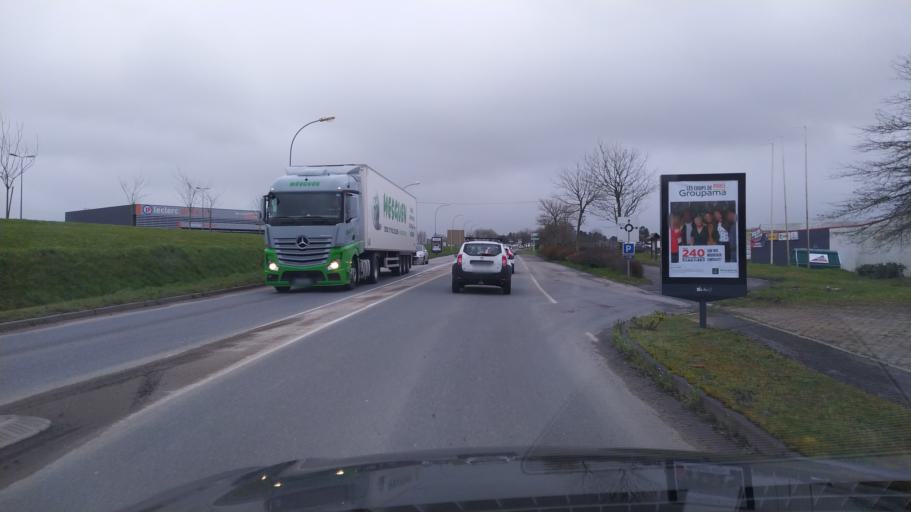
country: FR
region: Brittany
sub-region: Departement du Finistere
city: Landivisiau
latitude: 48.5221
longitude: -4.0603
